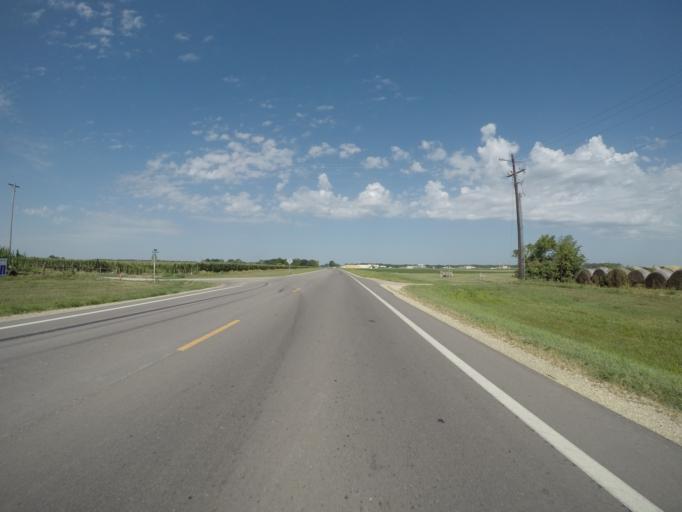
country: US
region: Kansas
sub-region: Clay County
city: Clay Center
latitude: 39.3800
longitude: -97.1555
